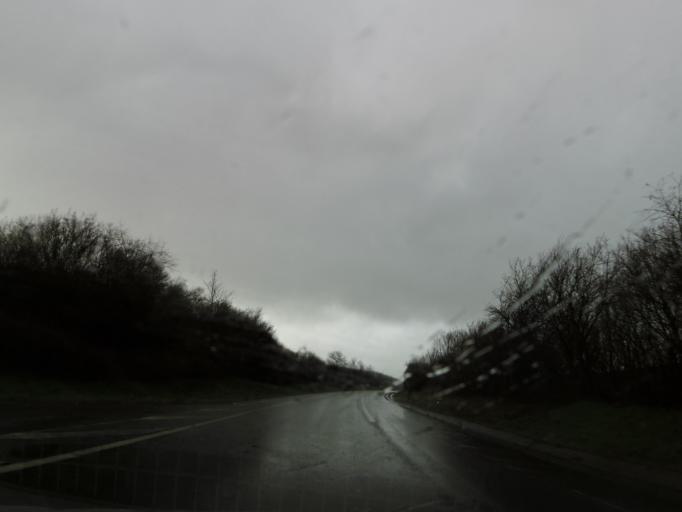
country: FR
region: Bourgogne
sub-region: Departement de Saone-et-Loire
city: Sance
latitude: 46.3501
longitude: 4.8280
